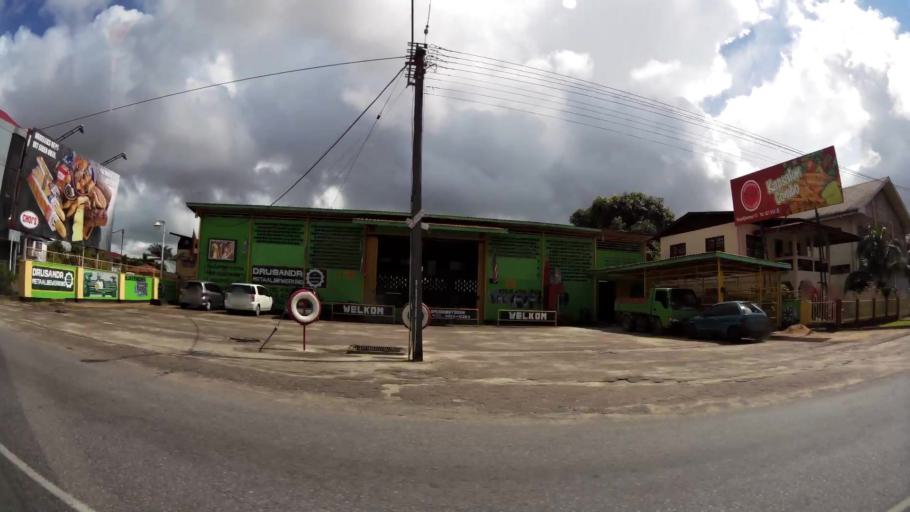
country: SR
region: Paramaribo
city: Paramaribo
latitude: 5.8322
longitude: -55.1878
